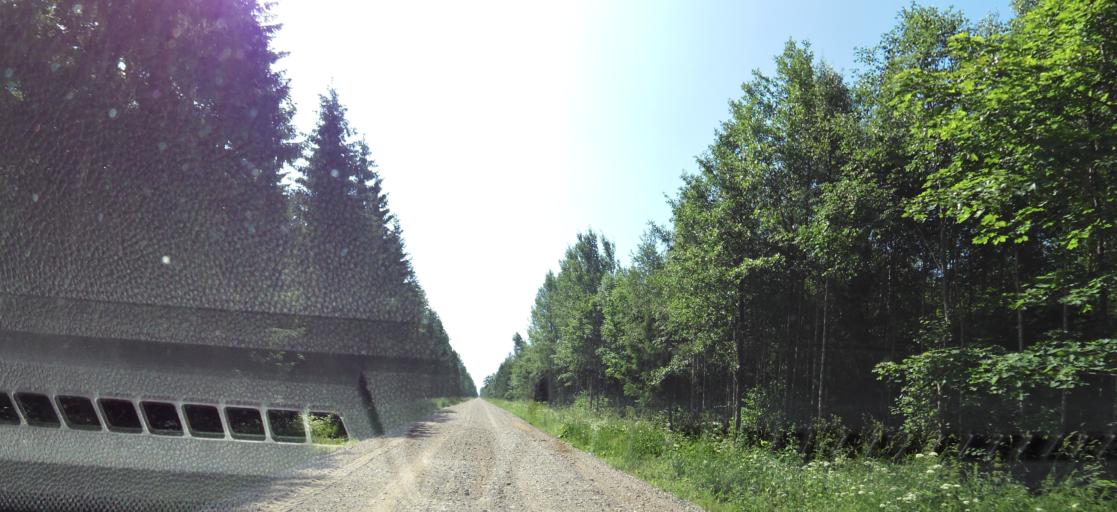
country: LT
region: Panevezys
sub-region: Birzai
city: Birzai
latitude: 56.2329
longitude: 24.9901
